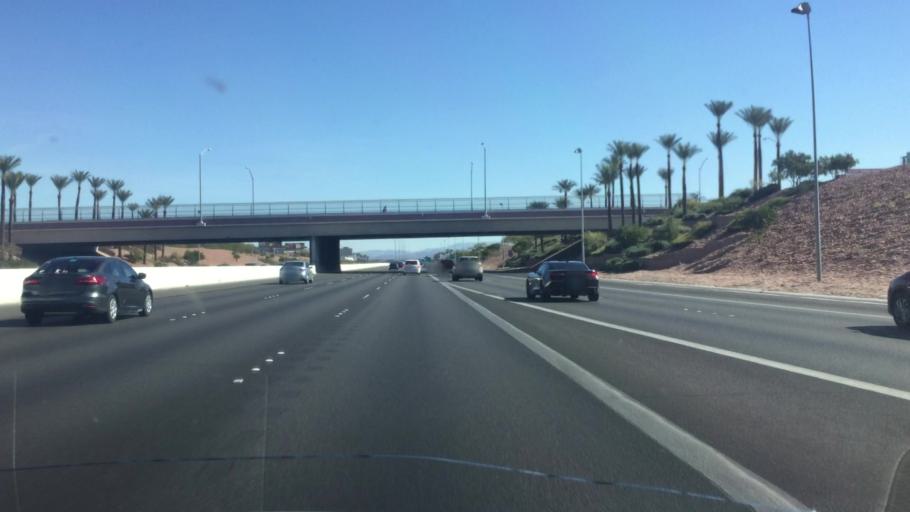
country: US
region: Nevada
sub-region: Clark County
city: Paradise
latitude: 36.0634
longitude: -115.1738
